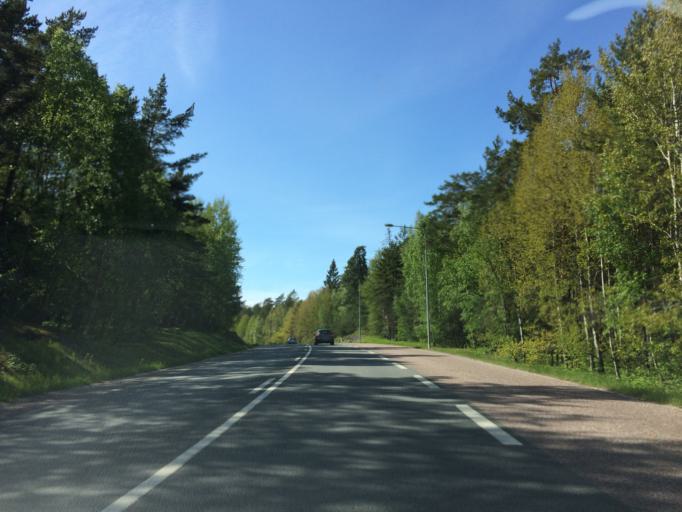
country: SE
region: Stockholm
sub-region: Sollentuna Kommun
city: Sollentuna
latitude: 59.4405
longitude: 17.9830
